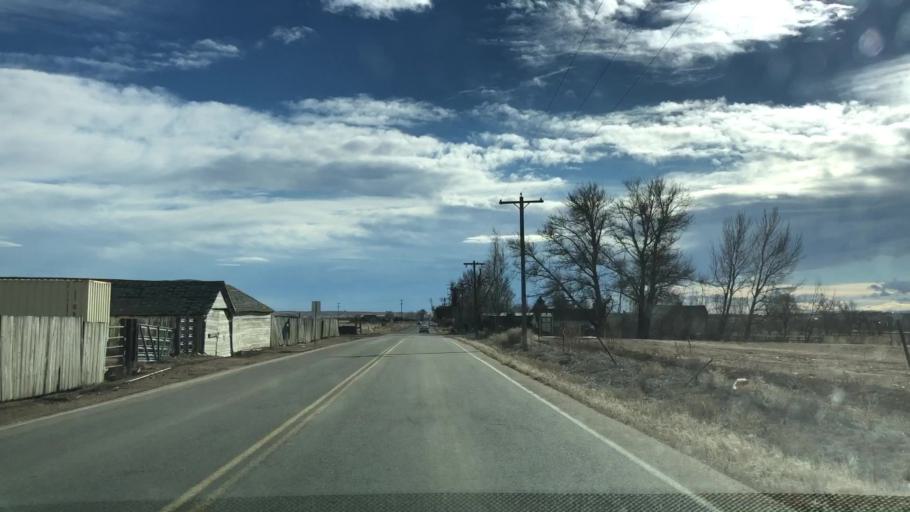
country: US
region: Colorado
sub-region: Weld County
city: Windsor
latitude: 40.5092
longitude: -104.9442
